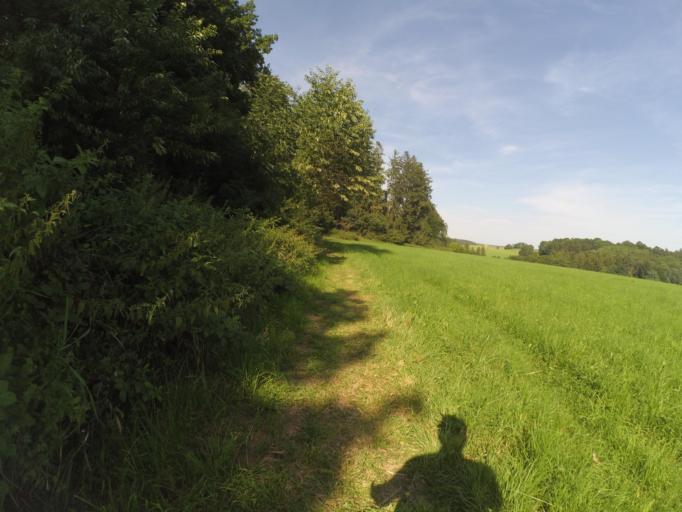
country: DE
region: Bavaria
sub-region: Swabia
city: Unteregg
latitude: 47.9701
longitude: 10.4549
